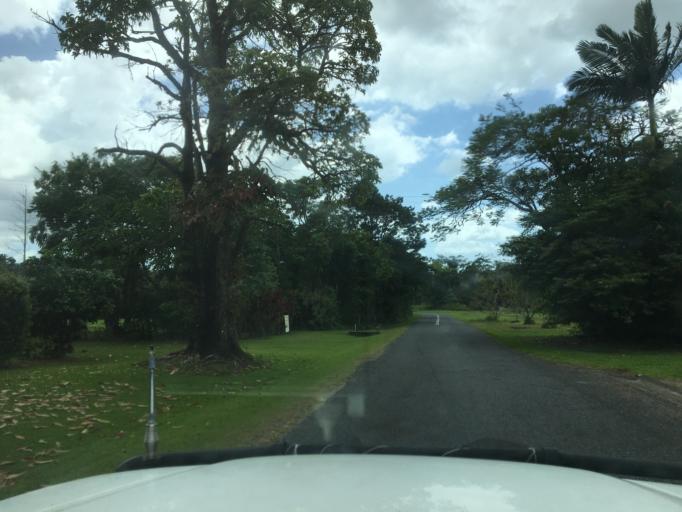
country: AU
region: Queensland
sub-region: Cairns
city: Woree
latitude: -17.2182
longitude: 145.9156
